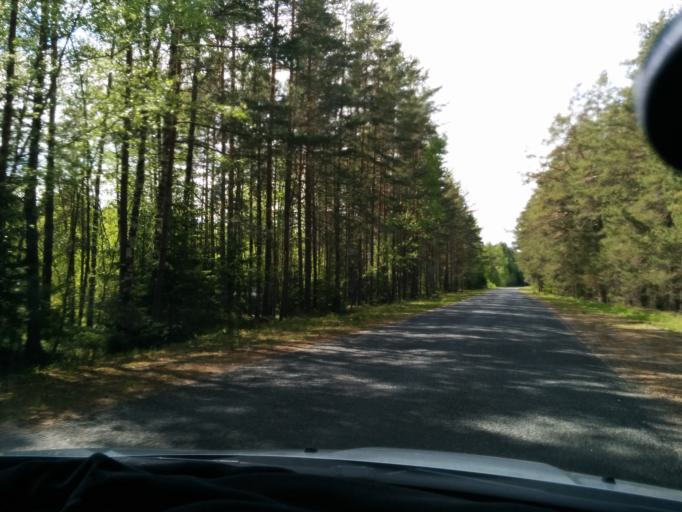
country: EE
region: Harju
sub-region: Loksa linn
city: Loksa
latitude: 59.5635
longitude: 25.6414
